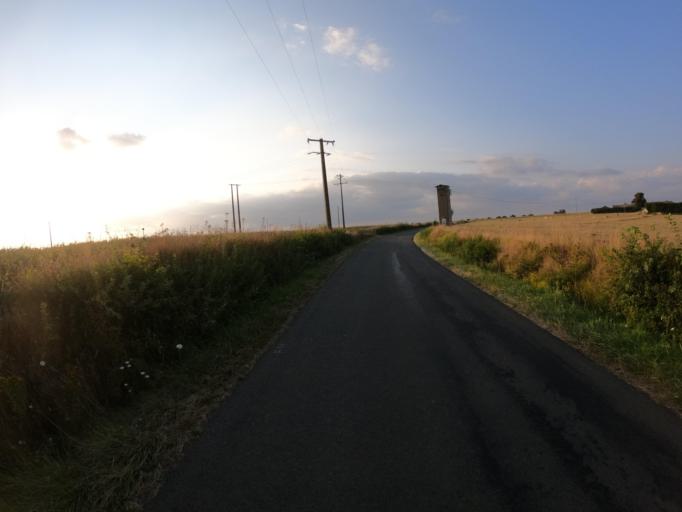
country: FR
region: Pays de la Loire
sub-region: Departement de la Sarthe
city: Brulon
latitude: 47.9168
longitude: -0.2293
